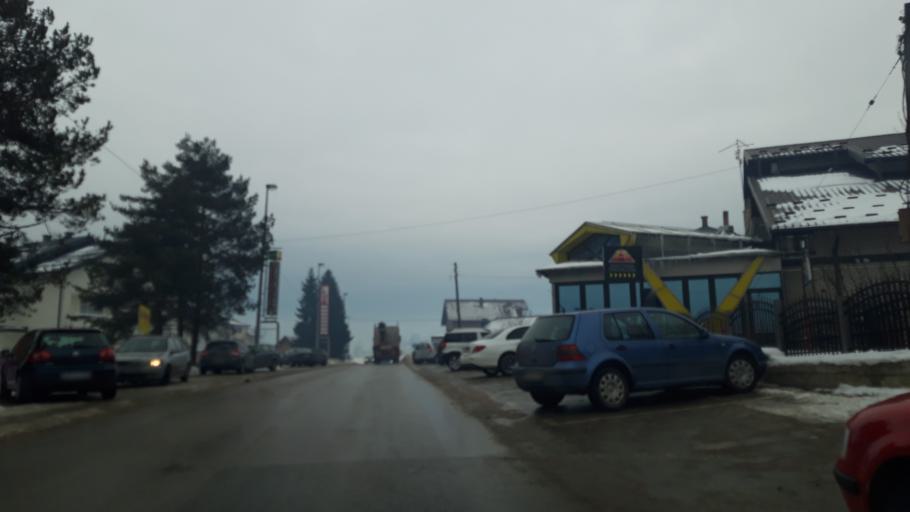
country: BA
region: Republika Srpska
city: Sokolac
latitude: 43.9351
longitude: 18.7915
